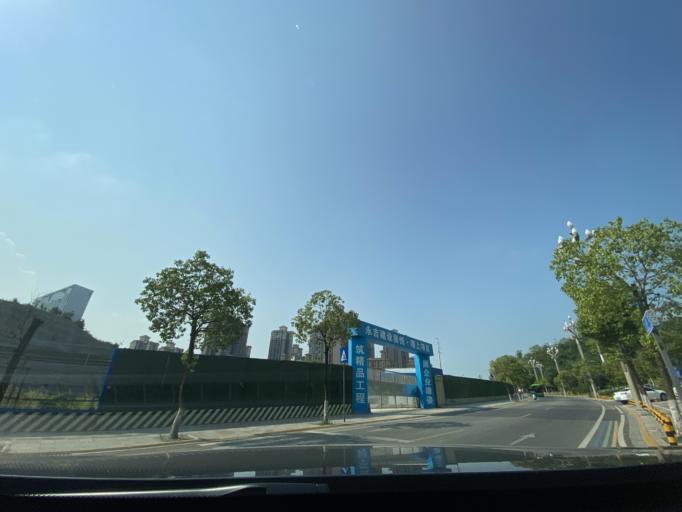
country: CN
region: Sichuan
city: Jiancheng
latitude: 30.4213
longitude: 104.5433
